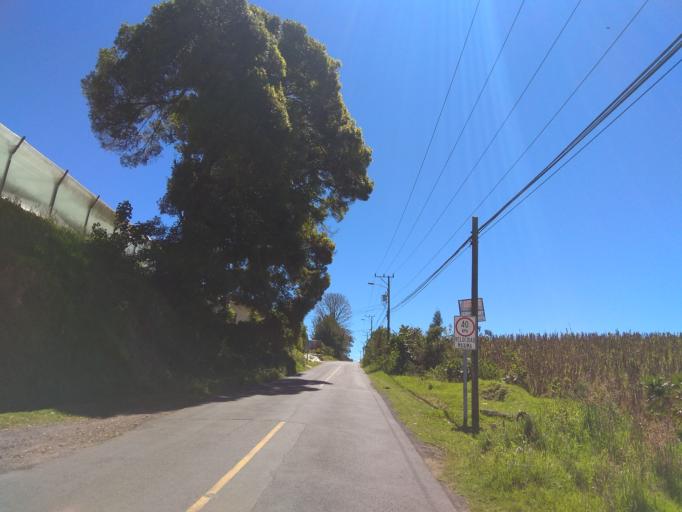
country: CR
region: Cartago
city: Cot
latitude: 9.9446
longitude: -83.9182
